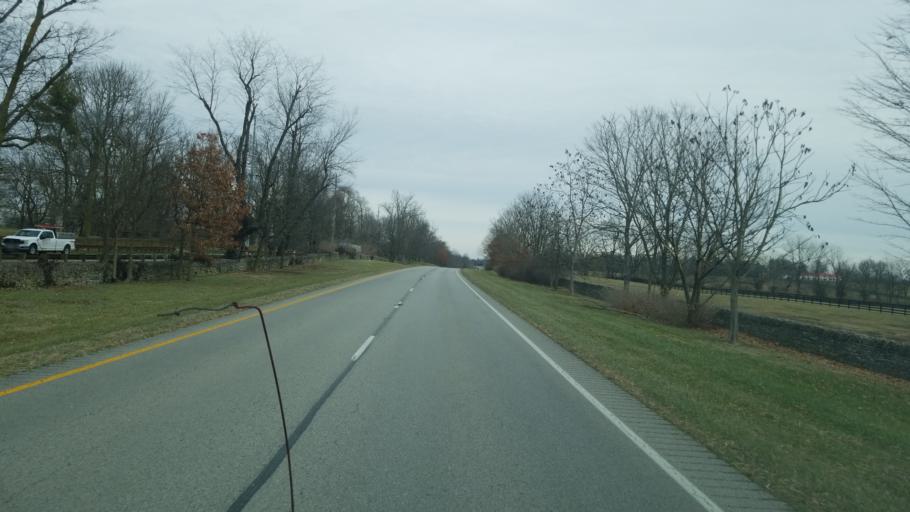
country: US
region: Kentucky
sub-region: Fayette County
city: Lexington-Fayette
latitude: 38.0998
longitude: -84.4183
